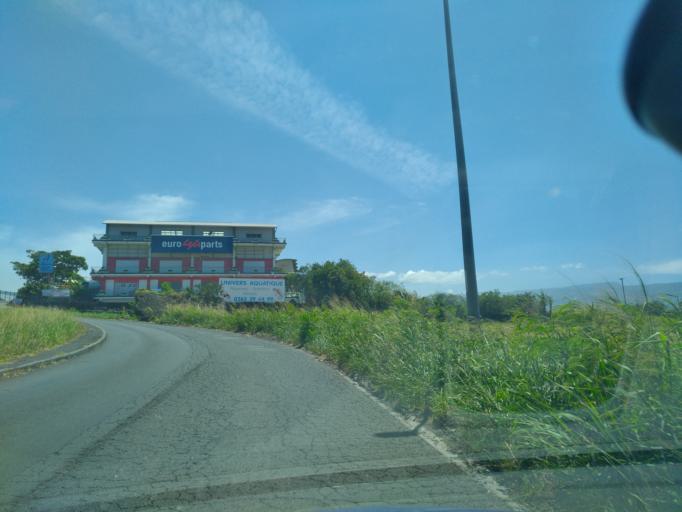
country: RE
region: Reunion
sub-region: Reunion
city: Saint-Pierre
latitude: -21.3228
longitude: 55.4487
